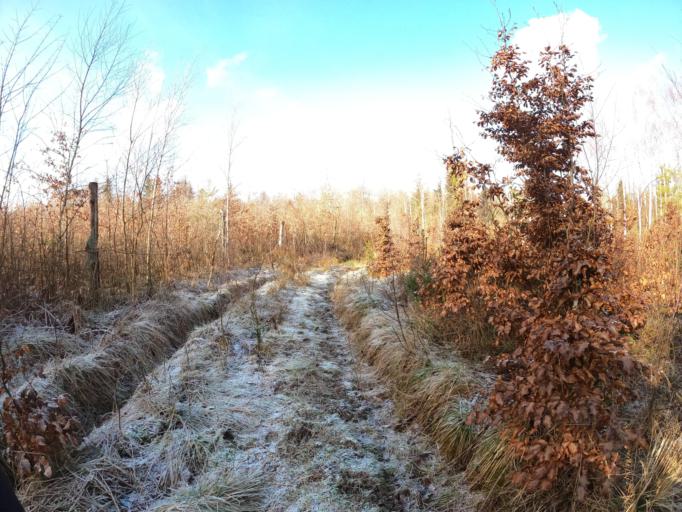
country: PL
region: West Pomeranian Voivodeship
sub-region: Powiat koszalinski
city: Polanow
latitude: 54.1323
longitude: 16.7755
